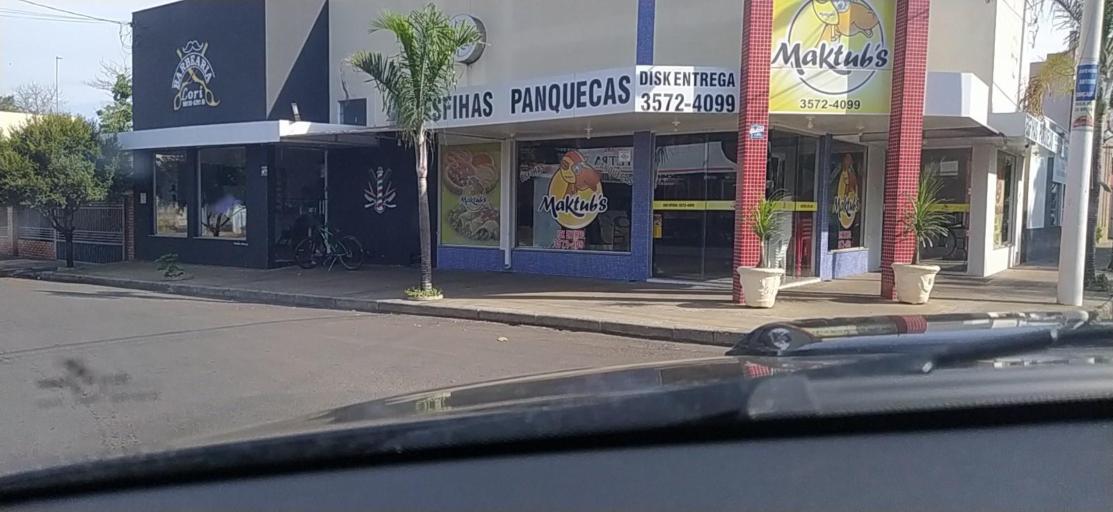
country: BR
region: Sao Paulo
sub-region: Pindorama
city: Pindorama
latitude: -21.1880
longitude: -48.9040
